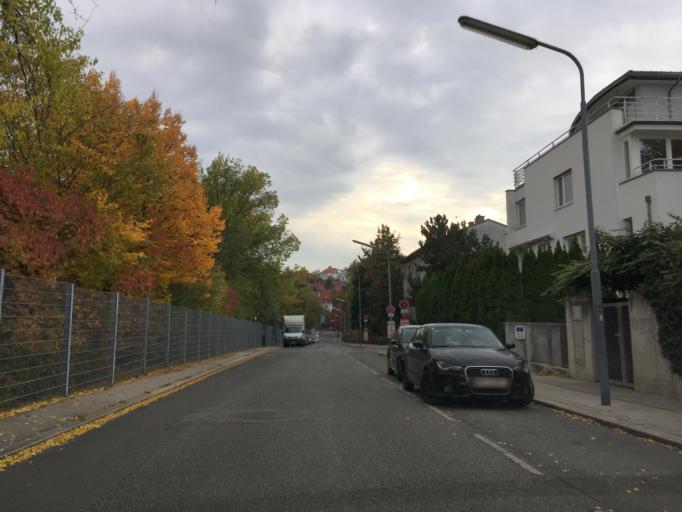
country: AT
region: Vienna
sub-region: Wien Stadt
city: Vienna
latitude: 48.2448
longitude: 16.3255
